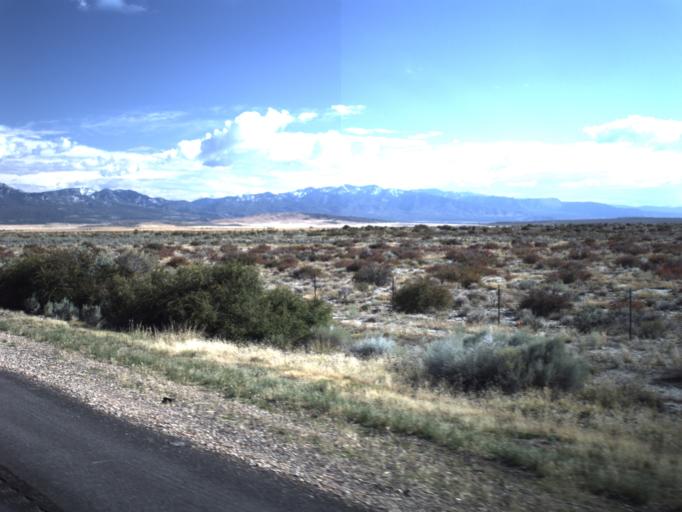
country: US
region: Utah
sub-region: Millard County
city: Fillmore
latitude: 39.1489
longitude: -112.3934
